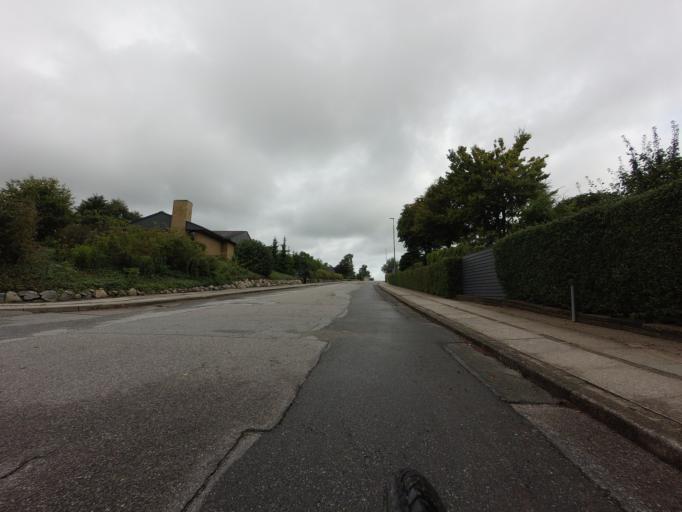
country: DK
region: North Denmark
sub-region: Hjorring Kommune
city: Hjorring
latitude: 57.4799
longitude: 9.9758
